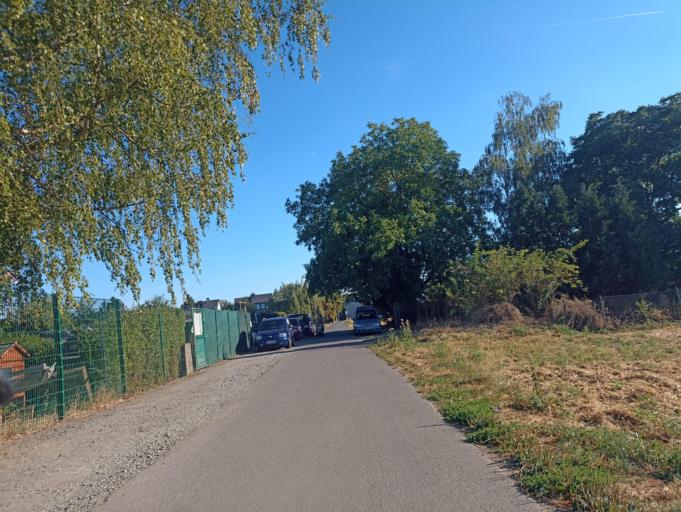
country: DE
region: Hesse
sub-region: Regierungsbezirk Darmstadt
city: Frankfurt am Main
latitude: 50.1684
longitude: 8.6542
